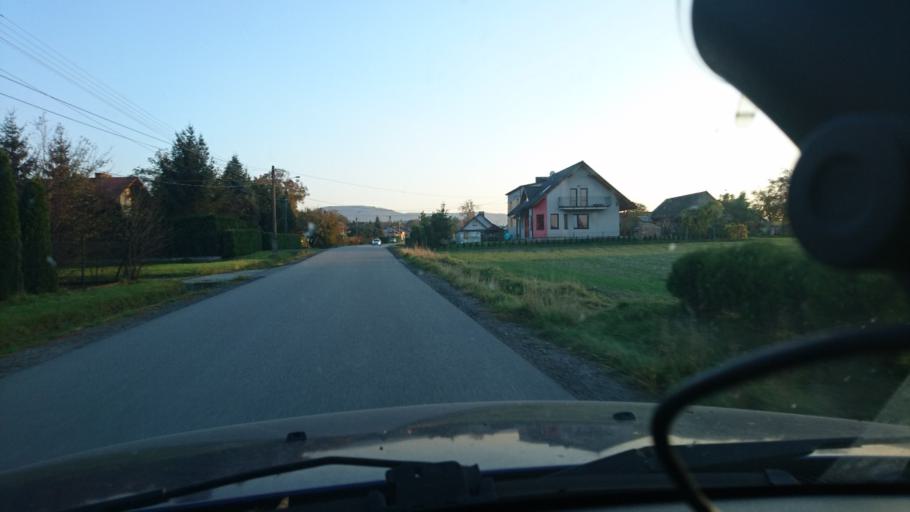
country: PL
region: Silesian Voivodeship
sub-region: Powiat bielski
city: Pisarzowice
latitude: 49.8724
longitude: 19.1405
